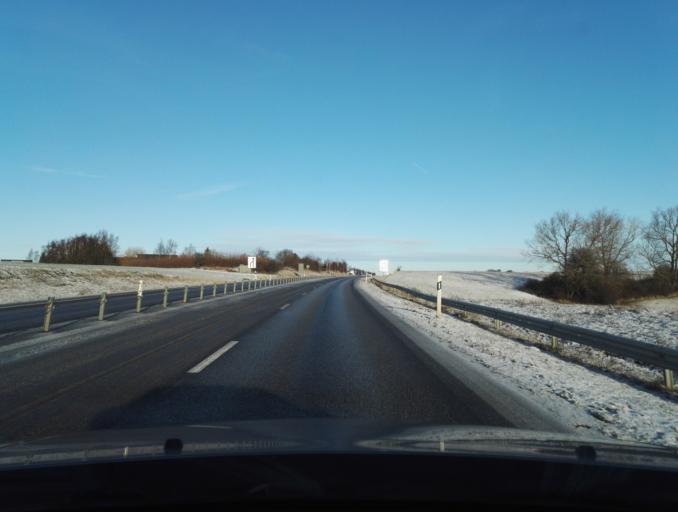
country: SE
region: Skane
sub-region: Svedala Kommun
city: Svedala
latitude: 55.4644
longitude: 13.1961
